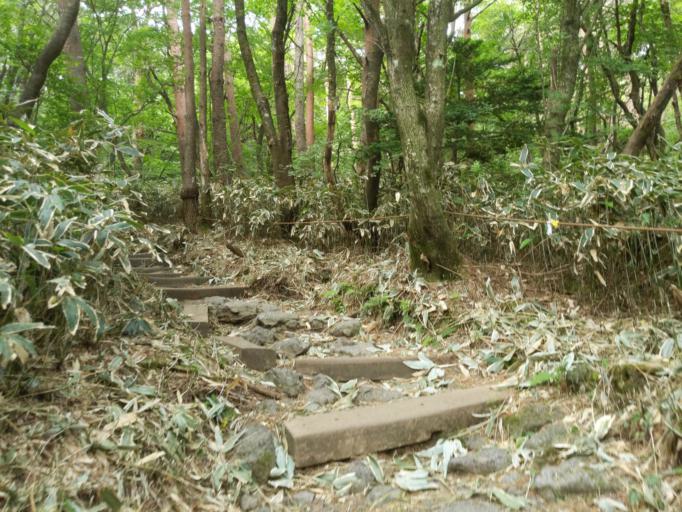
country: KR
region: Jeju-do
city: Jeju-si
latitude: 33.3881
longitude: 126.5374
